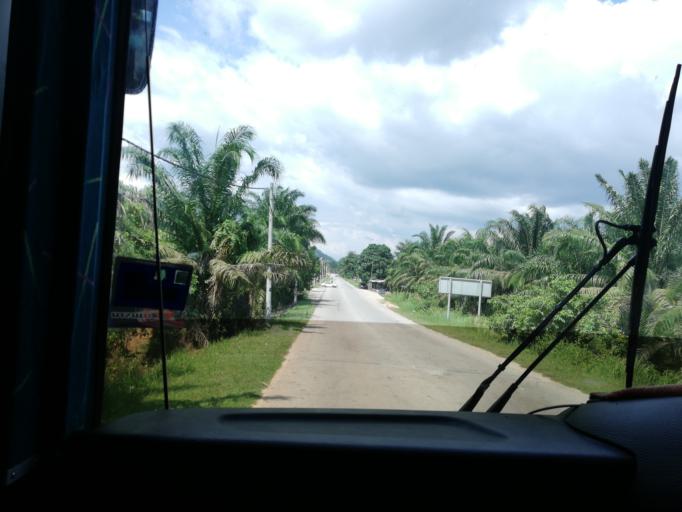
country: MY
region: Perak
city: Parit Buntar
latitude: 5.1121
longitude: 100.5553
